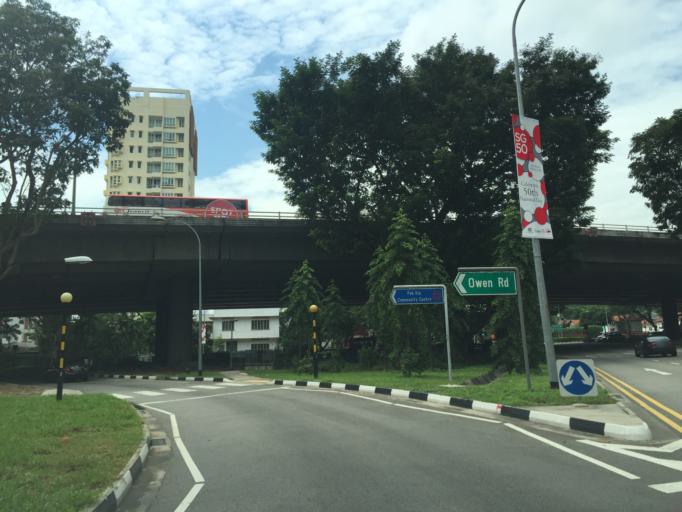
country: SG
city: Singapore
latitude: 1.3151
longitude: 103.8452
